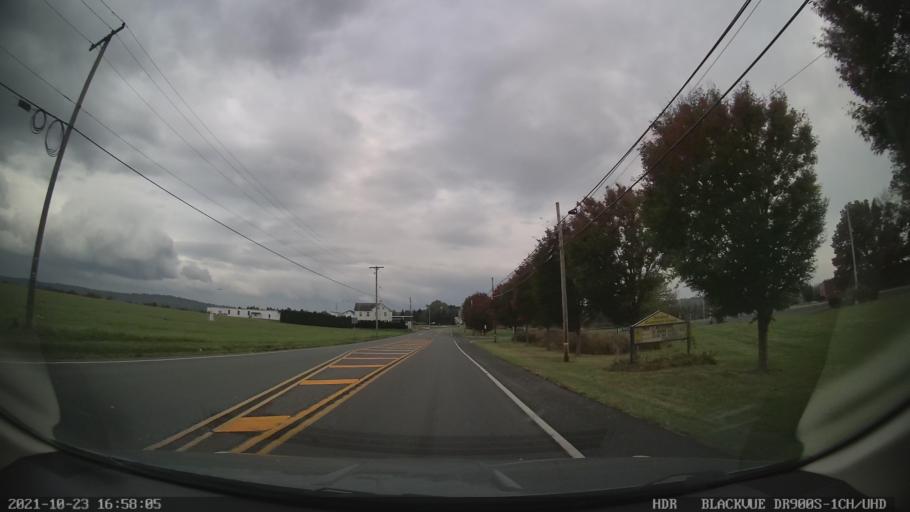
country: US
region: Pennsylvania
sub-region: Berks County
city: Bally
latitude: 40.4398
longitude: -75.5475
